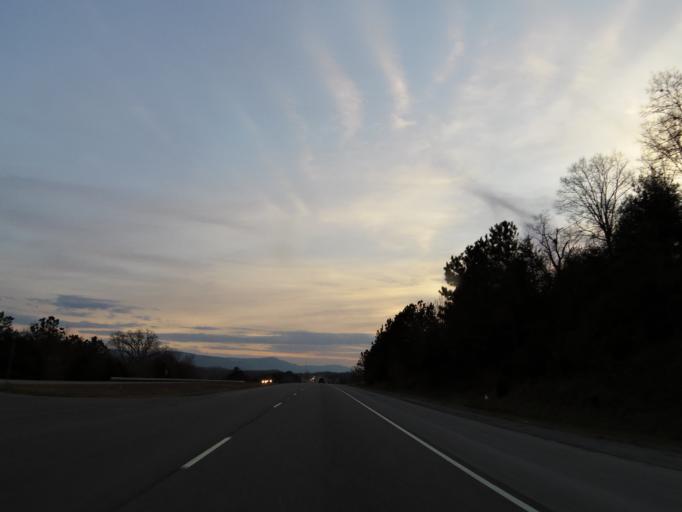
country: US
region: Tennessee
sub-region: McMinn County
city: Englewood
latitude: 35.3829
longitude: -84.5064
